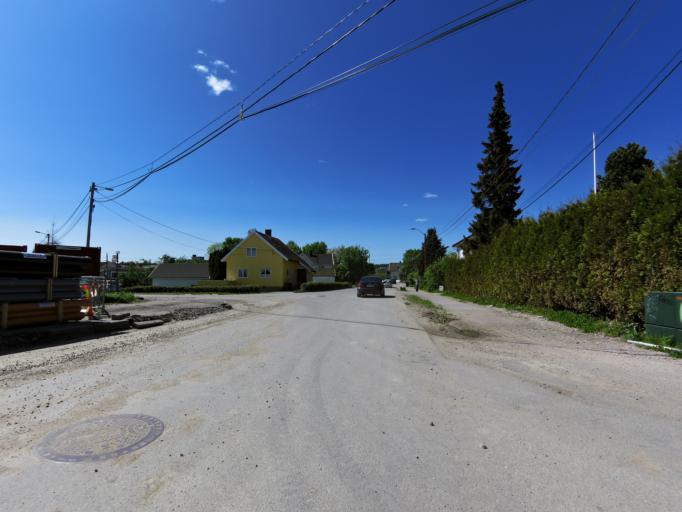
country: NO
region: Ostfold
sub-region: Fredrikstad
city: Fredrikstad
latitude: 59.2330
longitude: 10.9805
